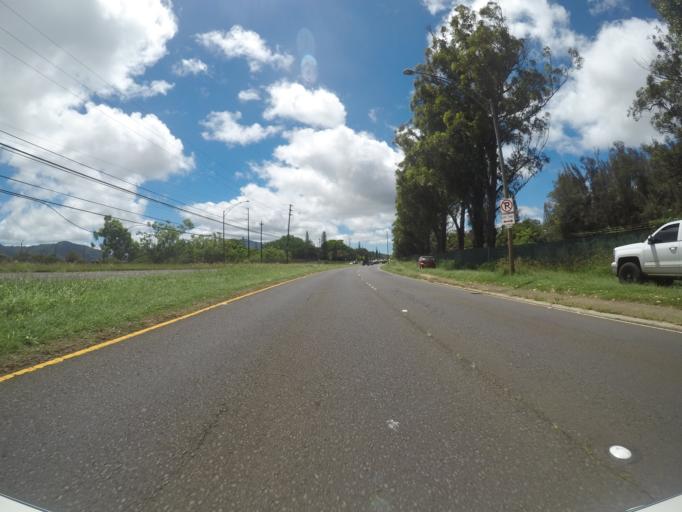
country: US
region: Hawaii
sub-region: Honolulu County
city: Wahiawa
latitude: 21.4892
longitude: -158.0431
